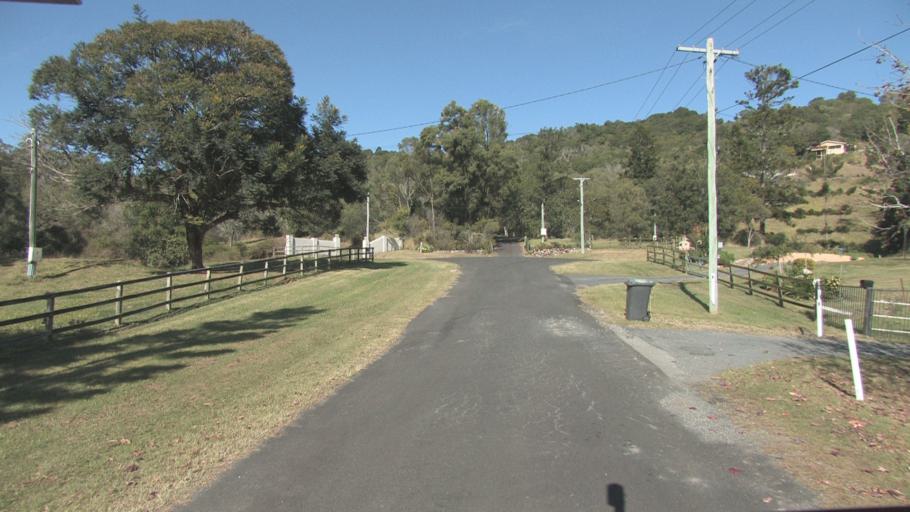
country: AU
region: Queensland
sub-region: Logan
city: Windaroo
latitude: -27.7443
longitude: 153.1722
